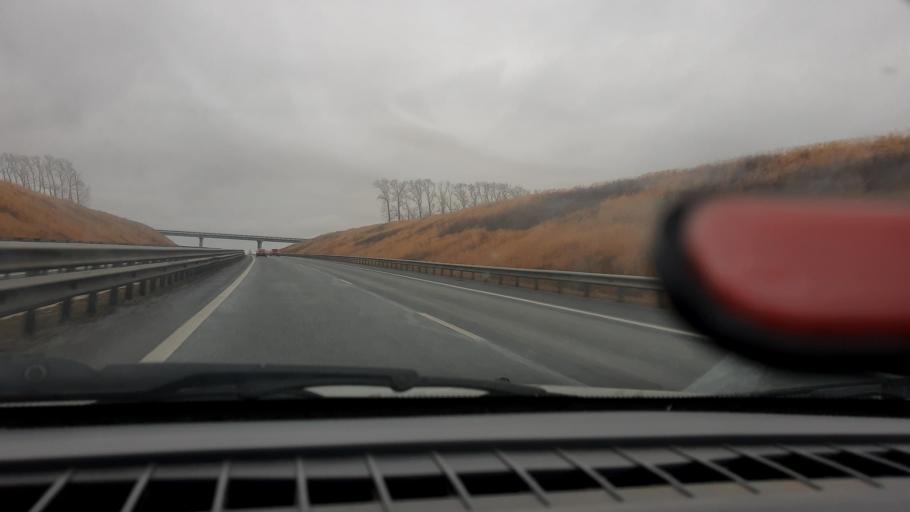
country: RU
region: Nizjnij Novgorod
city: Burevestnik
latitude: 56.1556
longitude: 43.7482
